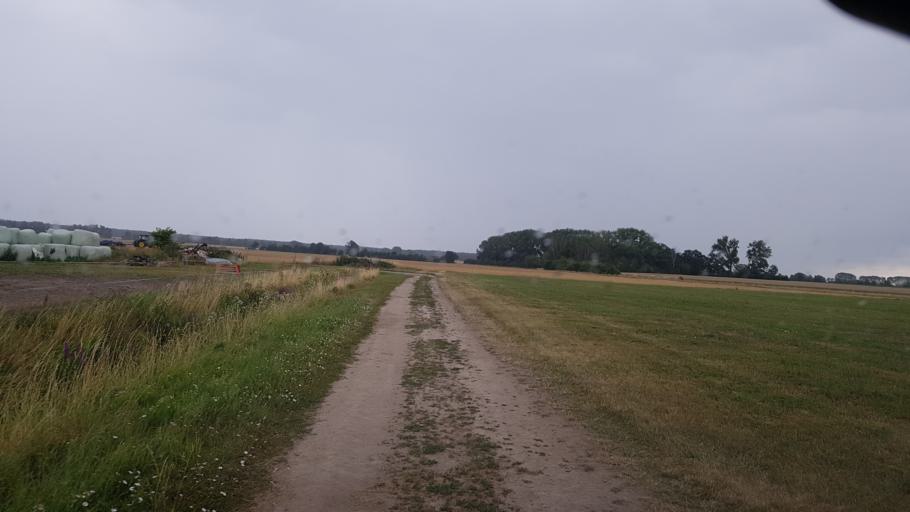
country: DE
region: Brandenburg
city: Sonnewalde
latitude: 51.7037
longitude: 13.6993
